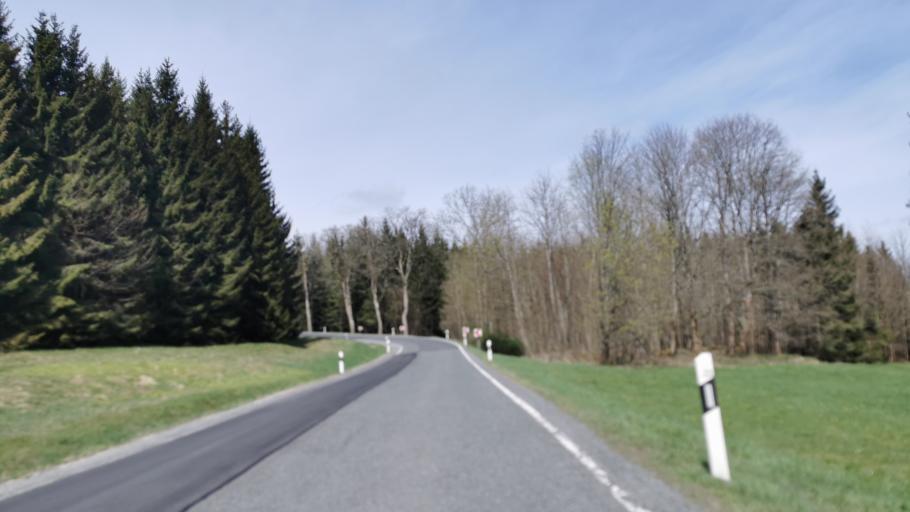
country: DE
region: Thuringia
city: Wurzbach
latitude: 50.4265
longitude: 11.5605
